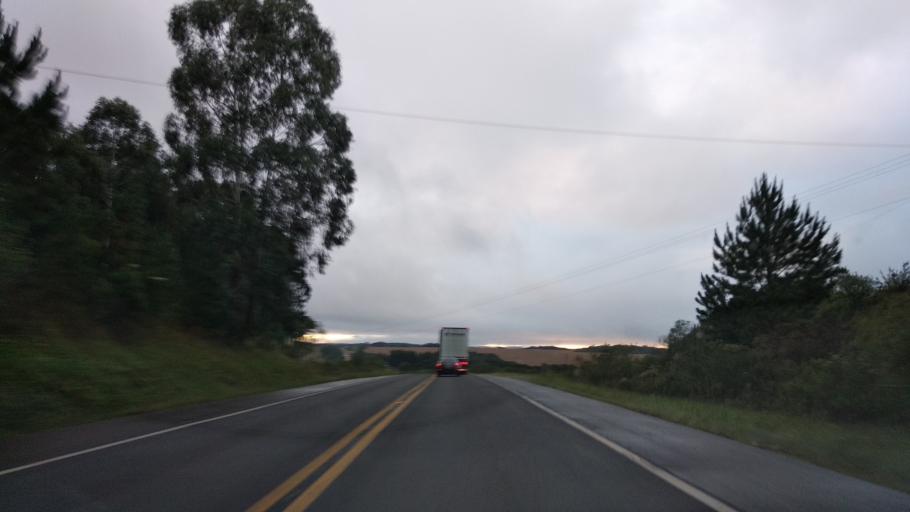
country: BR
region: Santa Catarina
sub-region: Campos Novos
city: Campos Novos
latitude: -27.3899
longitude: -51.1224
